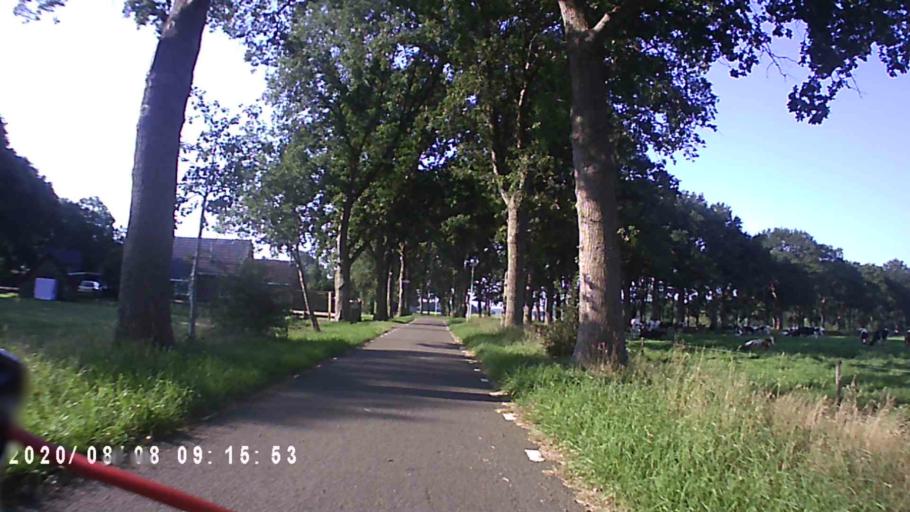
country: NL
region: Groningen
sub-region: Gemeente Leek
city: Leek
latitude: 53.0421
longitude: 6.3302
